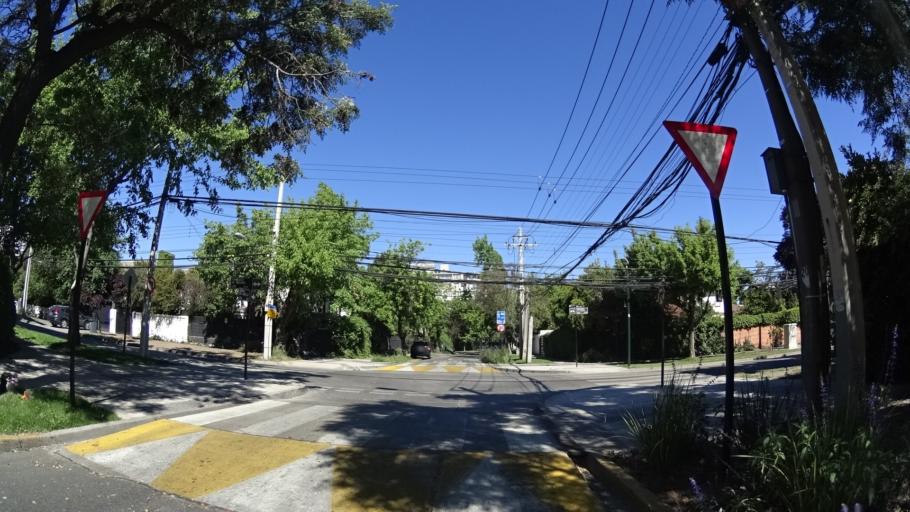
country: CL
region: Santiago Metropolitan
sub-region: Provincia de Santiago
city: Villa Presidente Frei, Nunoa, Santiago, Chile
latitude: -33.3936
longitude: -70.5938
